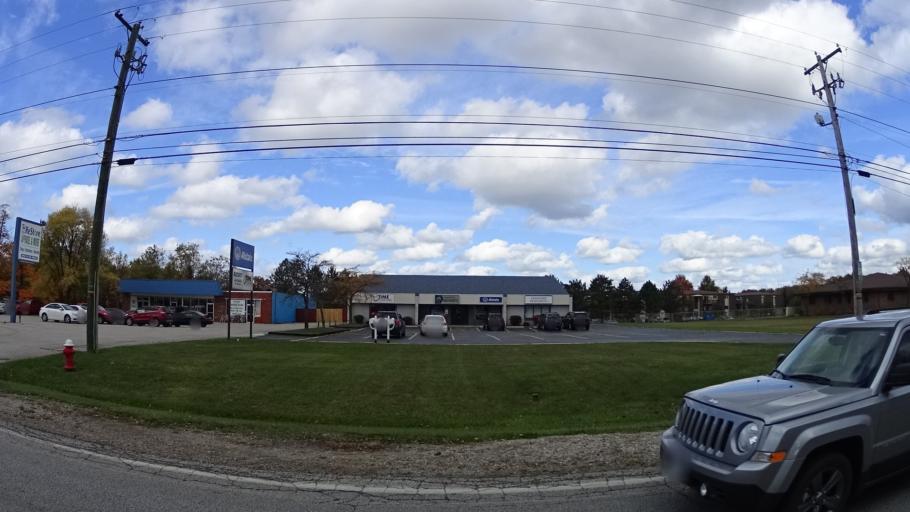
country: US
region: Ohio
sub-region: Lorain County
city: Lorain
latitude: 41.4183
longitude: -82.1887
